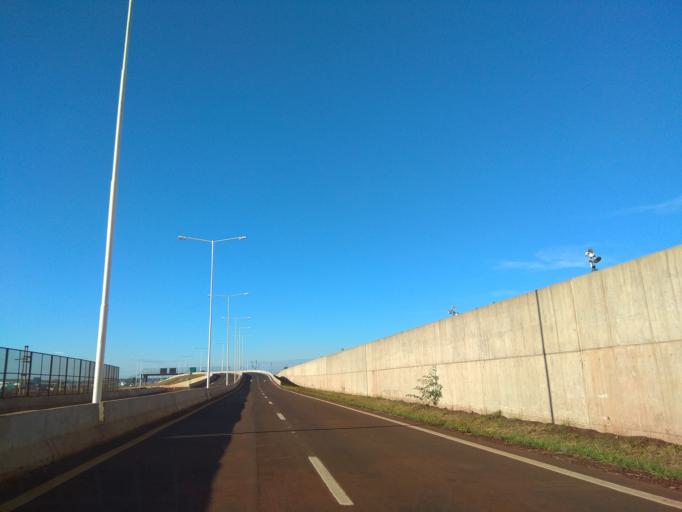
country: AR
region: Misiones
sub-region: Departamento de Capital
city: Posadas
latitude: -27.3773
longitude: -55.8845
